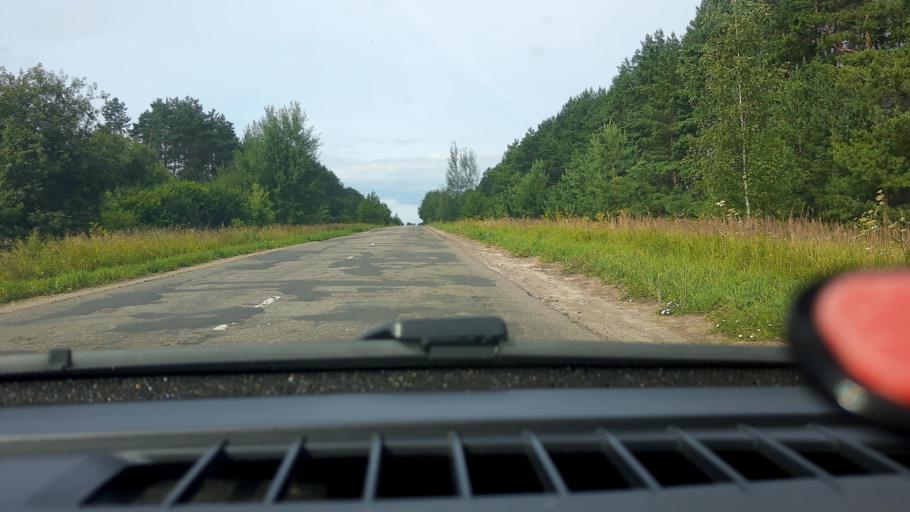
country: RU
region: Nizjnij Novgorod
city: Bogorodsk
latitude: 56.0653
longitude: 43.6163
